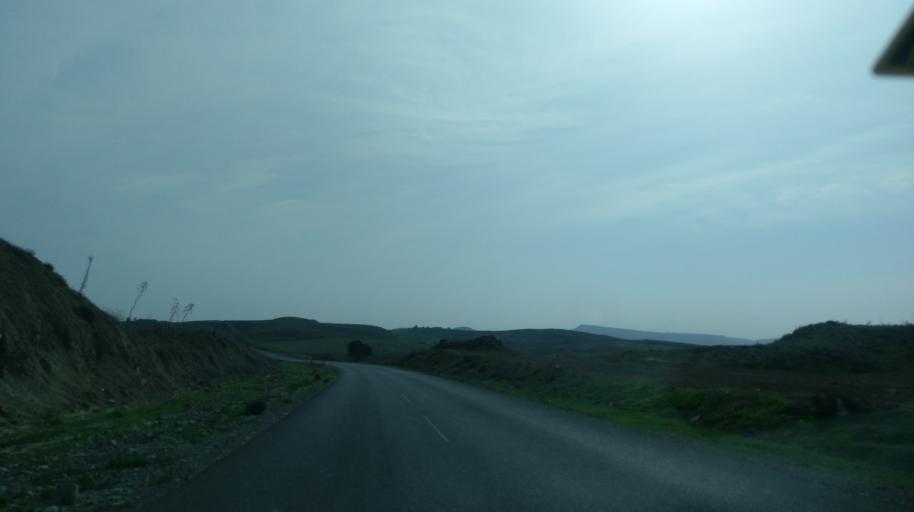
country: CY
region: Keryneia
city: Lapithos
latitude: 35.2831
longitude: 33.0950
